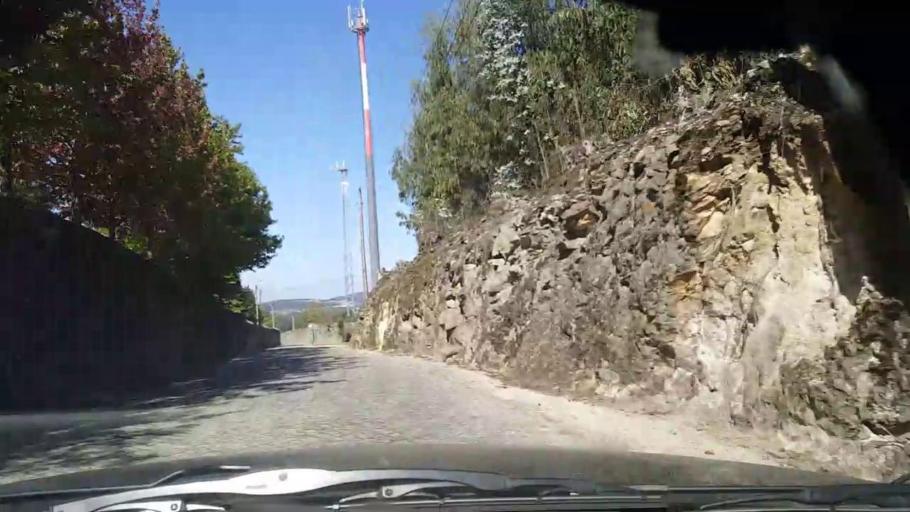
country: PT
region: Porto
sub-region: Vila do Conde
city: Arvore
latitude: 41.3285
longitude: -8.6721
